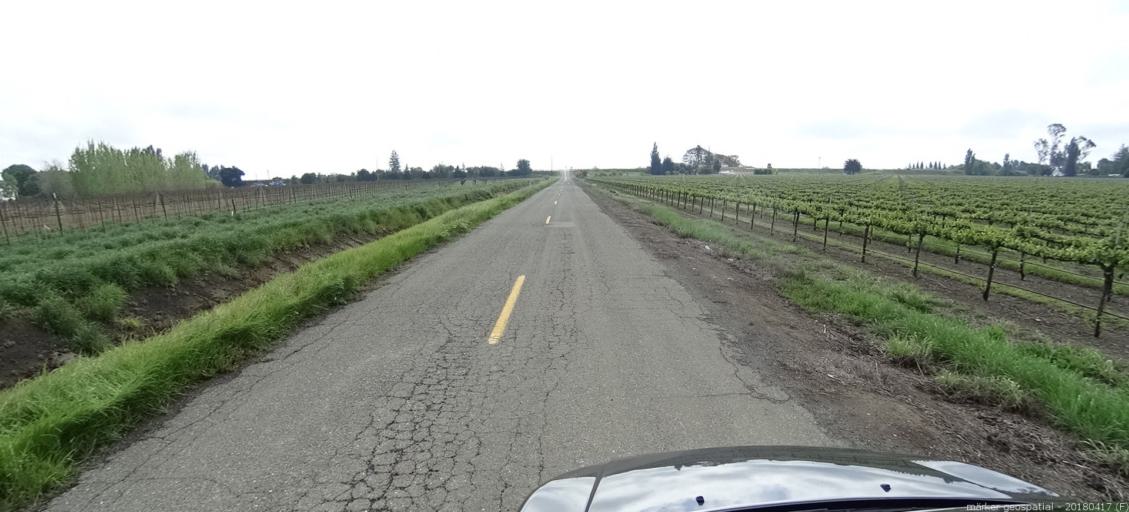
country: US
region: California
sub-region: Sacramento County
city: Walnut Grove
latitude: 38.2130
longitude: -121.5626
